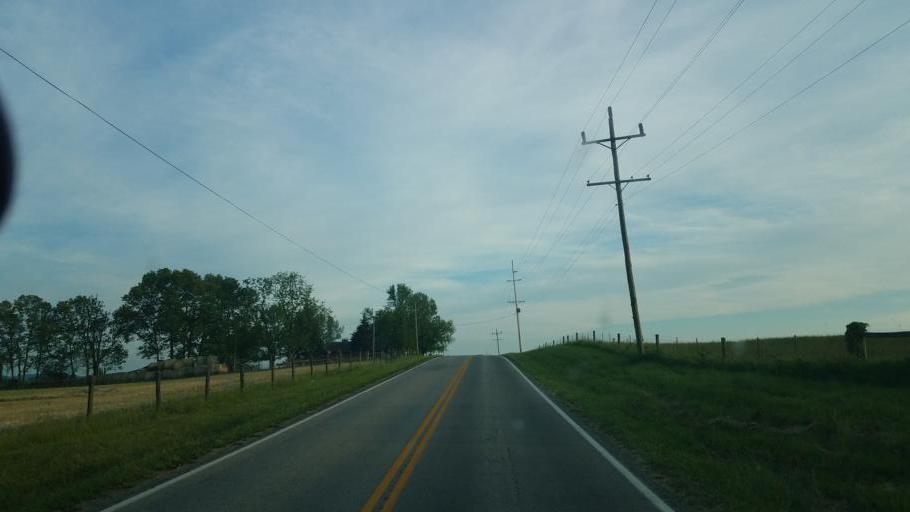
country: US
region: Ohio
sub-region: Highland County
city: Greenfield
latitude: 39.3007
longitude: -83.4087
